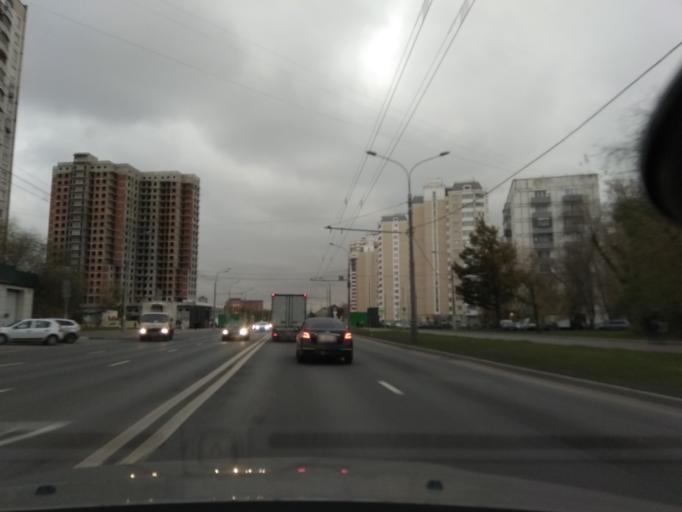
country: RU
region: Moscow
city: Novovladykino
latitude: 55.8251
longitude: 37.5843
